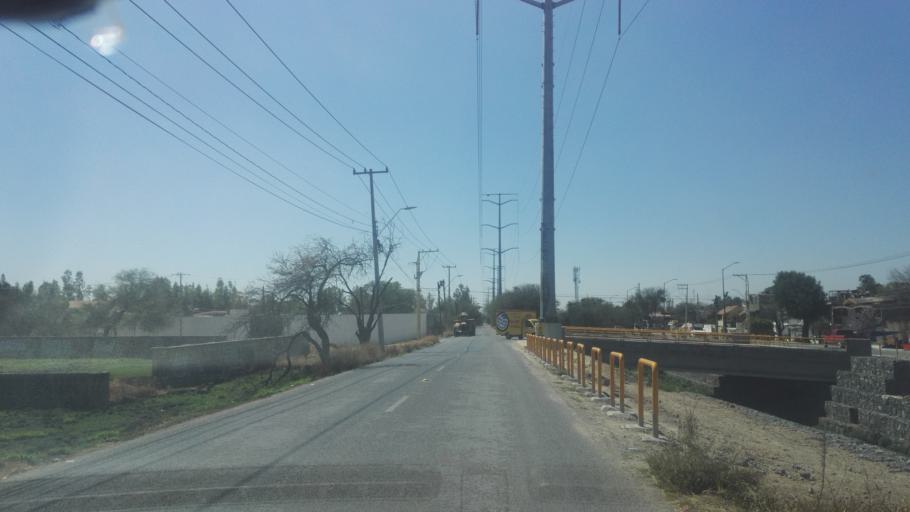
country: MX
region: Guanajuato
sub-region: Leon
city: Fraccionamiento Paraiso Real
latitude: 21.0731
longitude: -101.6009
